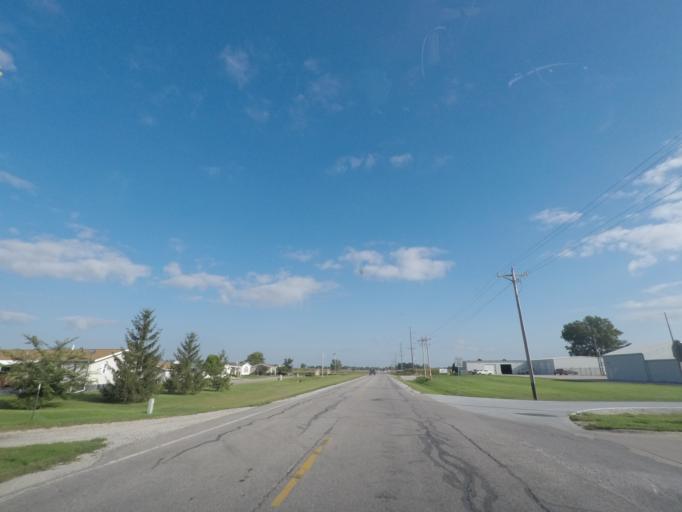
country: US
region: Iowa
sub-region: Story County
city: Nevada
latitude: 42.0008
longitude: -93.4629
